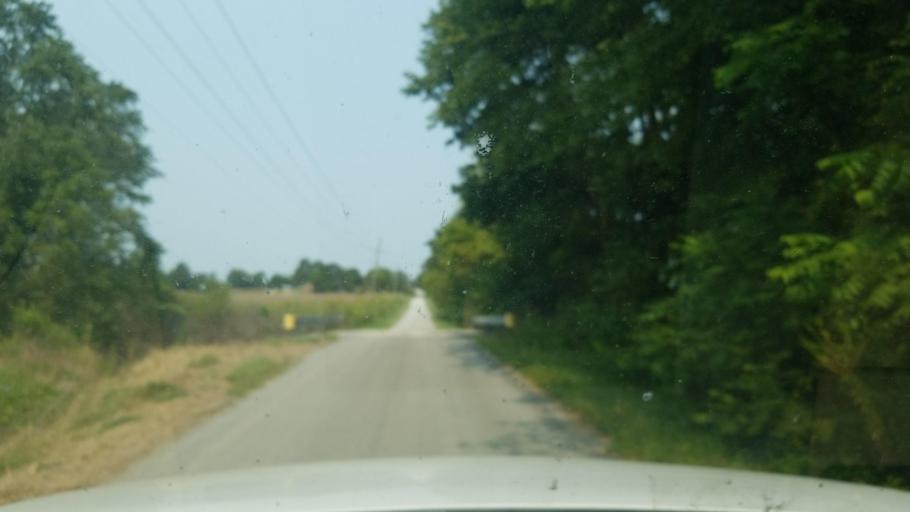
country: US
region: Illinois
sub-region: Saline County
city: Harrisburg
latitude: 37.8102
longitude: -88.5167
